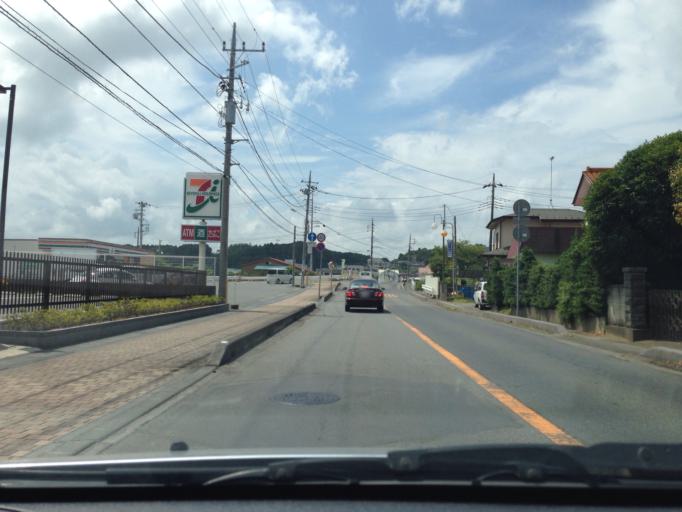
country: JP
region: Ibaraki
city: Ami
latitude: 36.0692
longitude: 140.2112
